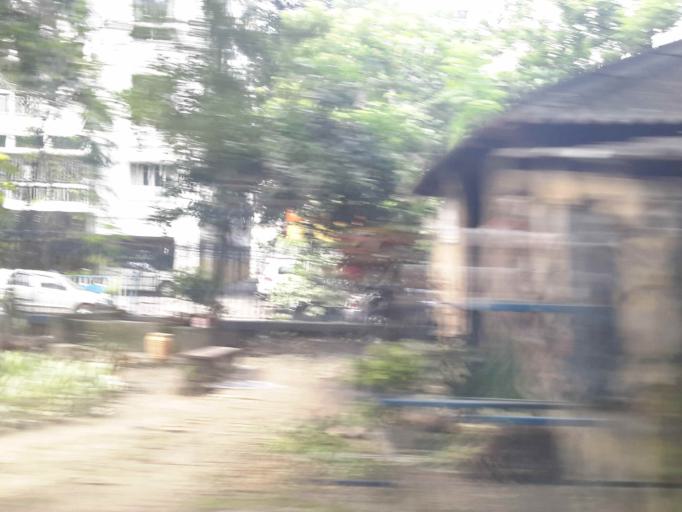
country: IN
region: West Bengal
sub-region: Kolkata
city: Kolkata
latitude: 22.5139
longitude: 88.3616
